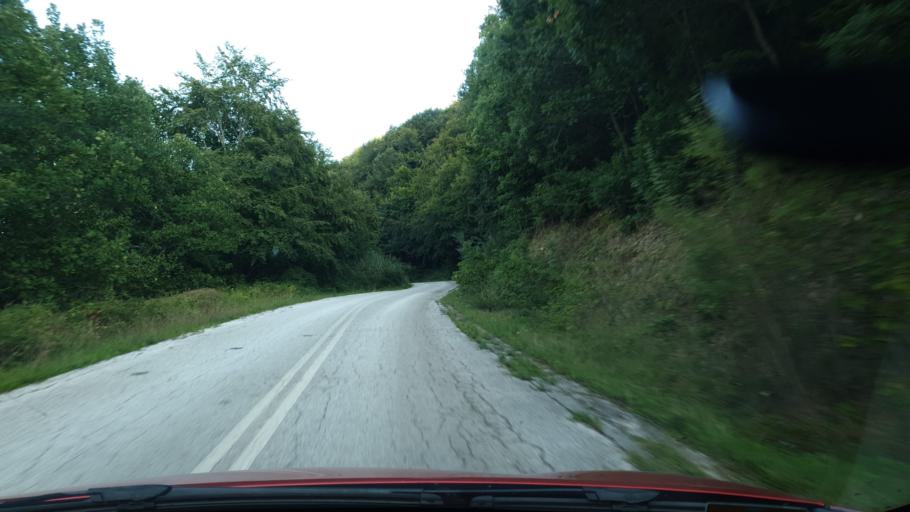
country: GR
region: Central Macedonia
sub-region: Nomos Chalkidikis
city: Galatista
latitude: 40.5105
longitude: 23.2531
